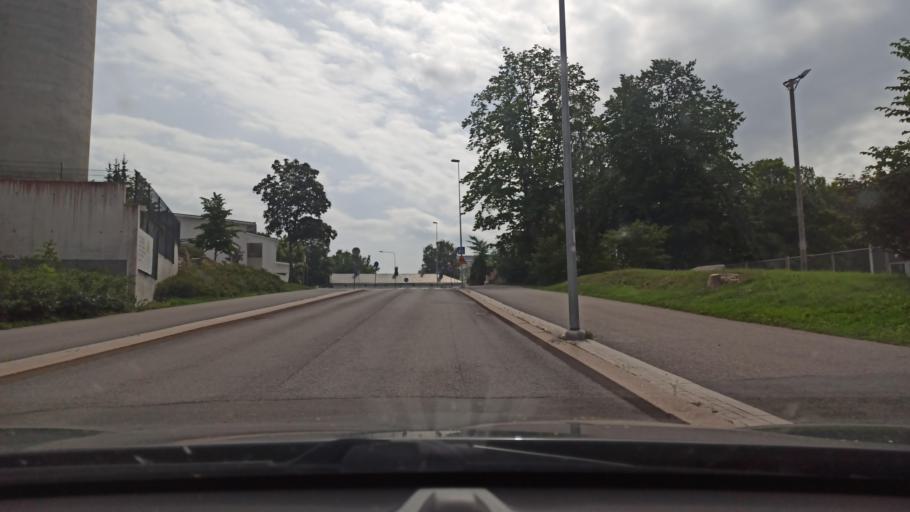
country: FI
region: Varsinais-Suomi
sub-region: Turku
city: Turku
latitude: 60.4436
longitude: 22.2376
